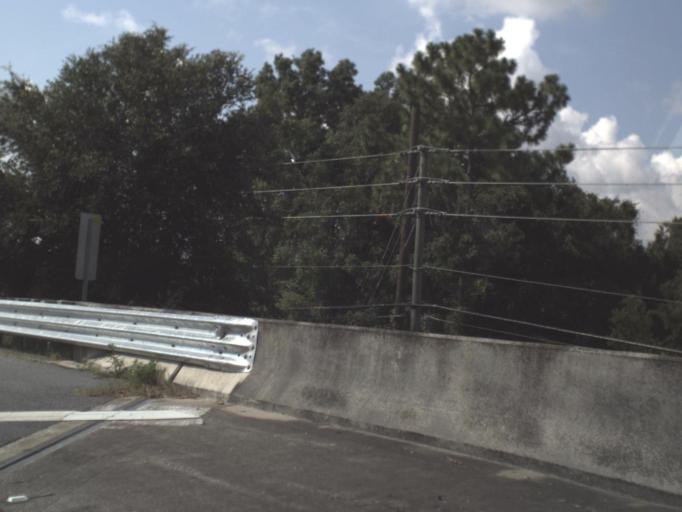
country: US
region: Florida
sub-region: Marion County
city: Dunnellon
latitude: 29.0408
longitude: -82.4660
